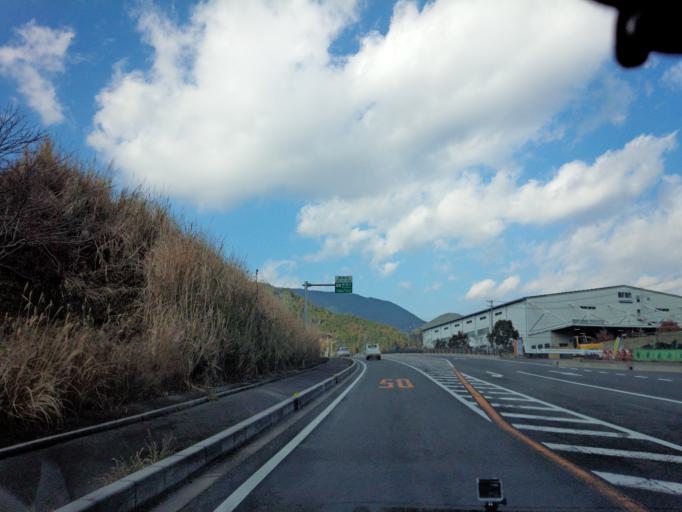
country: JP
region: Shizuoka
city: Fujinomiya
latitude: 35.1502
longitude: 138.5229
